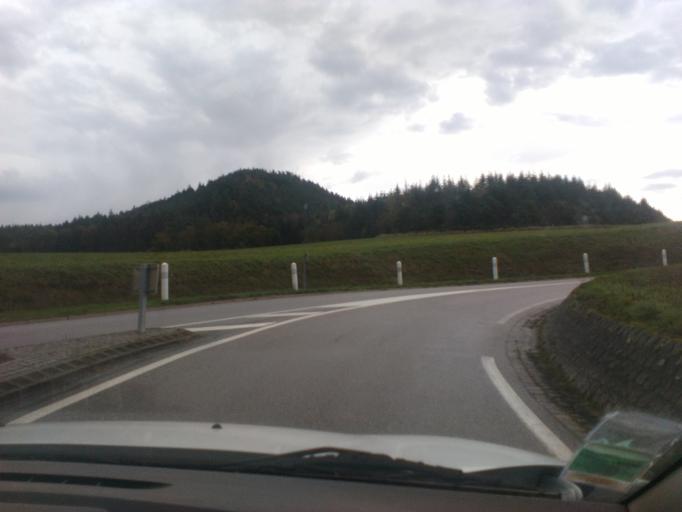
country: FR
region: Lorraine
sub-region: Departement des Vosges
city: Bruyeres
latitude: 48.1908
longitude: 6.7403
